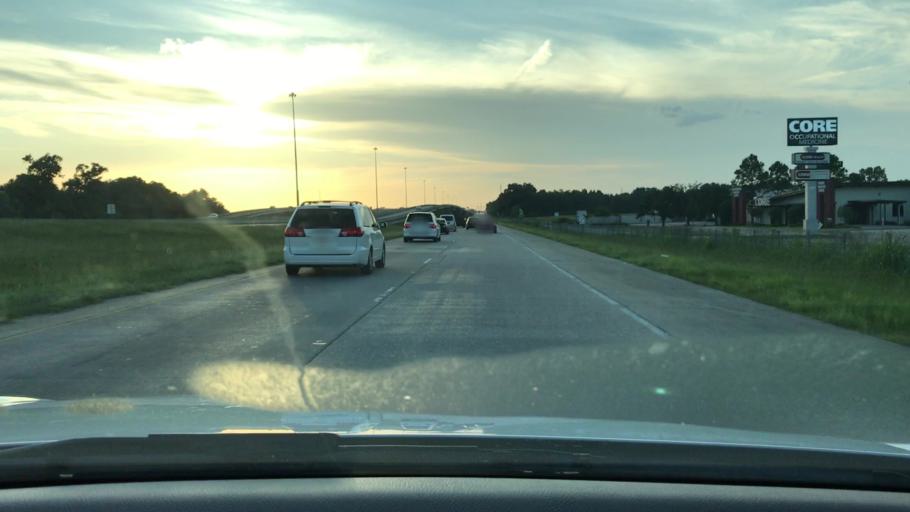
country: US
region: Louisiana
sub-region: East Baton Rouge Parish
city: Village Saint George
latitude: 30.3841
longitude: -91.0677
